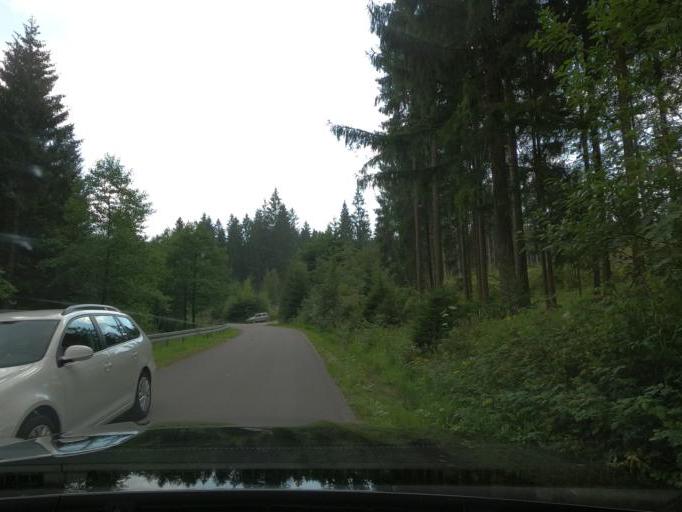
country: DE
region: Lower Saxony
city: Clausthal-Zellerfeld
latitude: 51.7840
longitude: 10.2996
